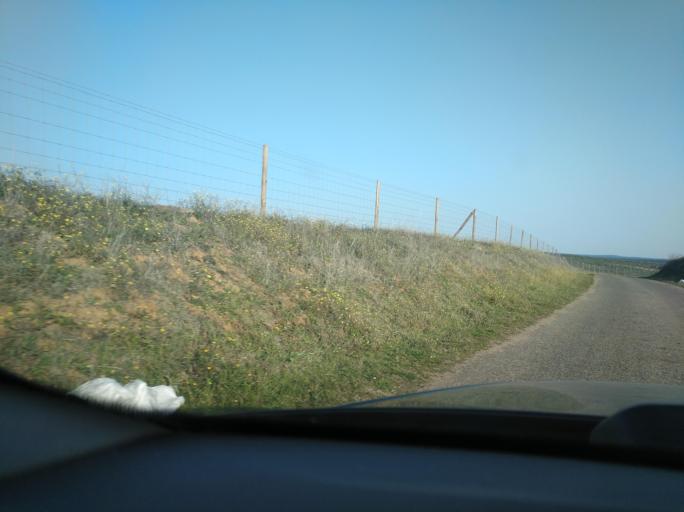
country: PT
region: Portalegre
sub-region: Campo Maior
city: Campo Maior
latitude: 39.0087
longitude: -7.0258
